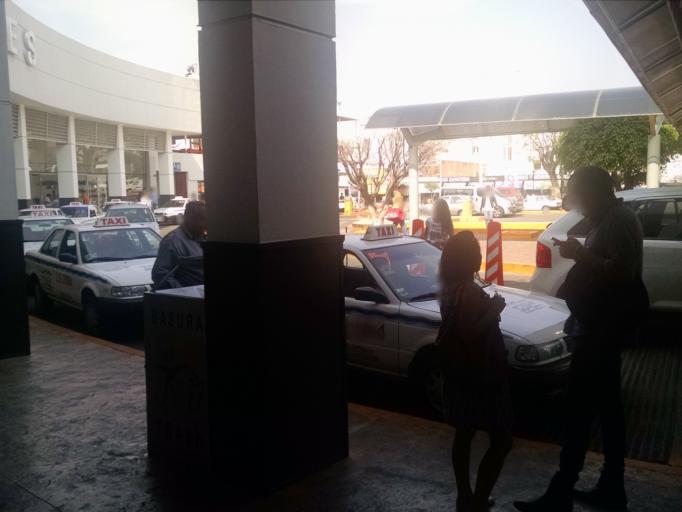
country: MX
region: Guanajuato
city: Leon
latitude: 21.1210
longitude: -101.6618
